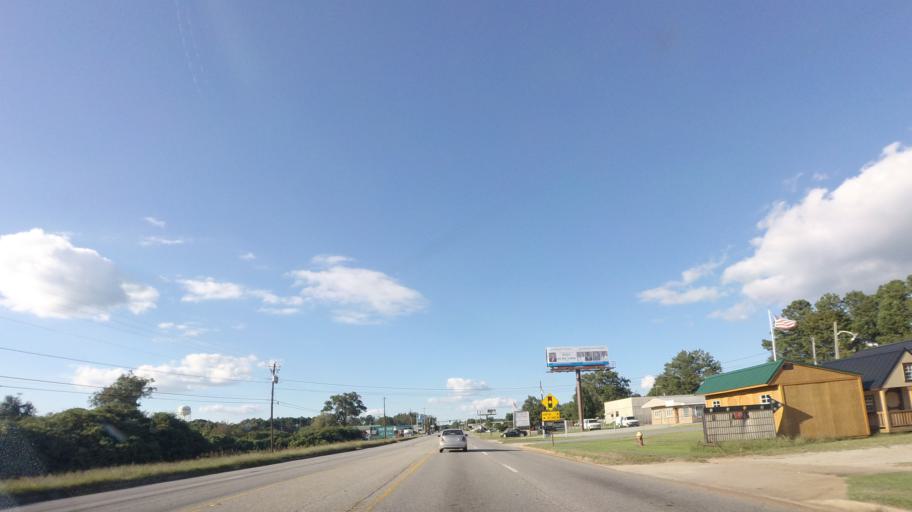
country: US
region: Georgia
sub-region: Upson County
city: Hannahs Mill
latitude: 32.9327
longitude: -84.3340
